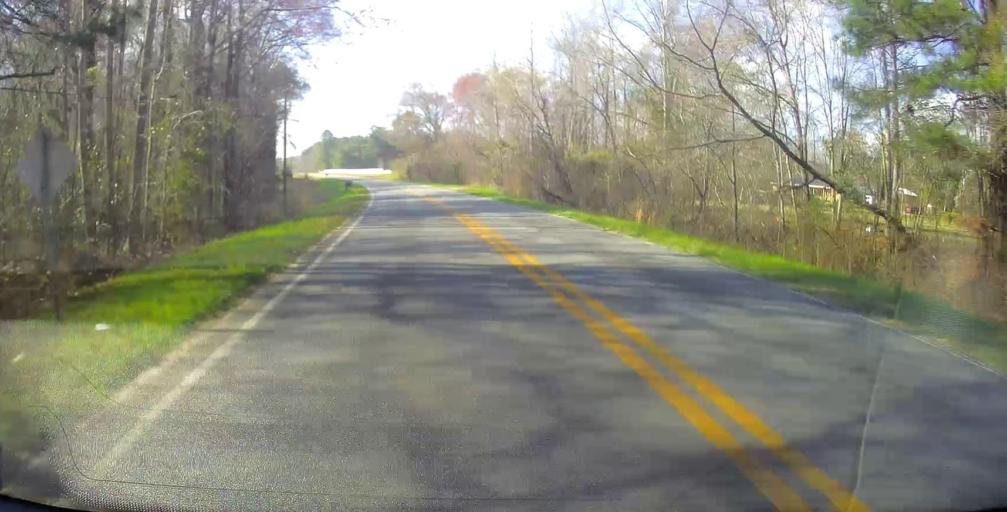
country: US
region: Georgia
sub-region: Laurens County
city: Dublin
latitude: 32.5558
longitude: -82.9968
